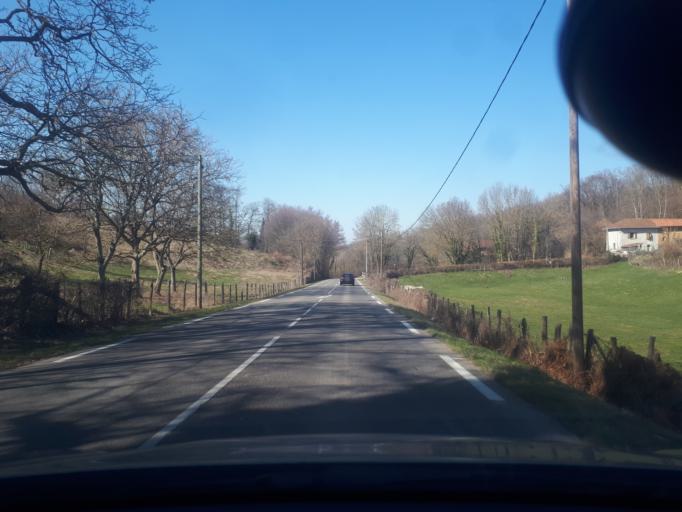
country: FR
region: Rhone-Alpes
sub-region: Departement de l'Isere
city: La Cote-Saint-Andre
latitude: 45.4081
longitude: 5.2702
